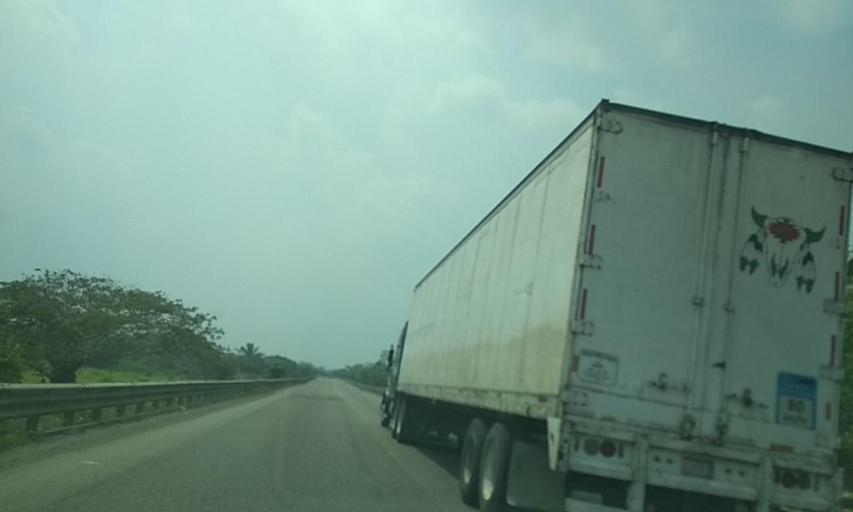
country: MX
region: Tabasco
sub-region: Huimanguillo
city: Francisco Rueda
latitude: 17.7581
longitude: -94.0055
